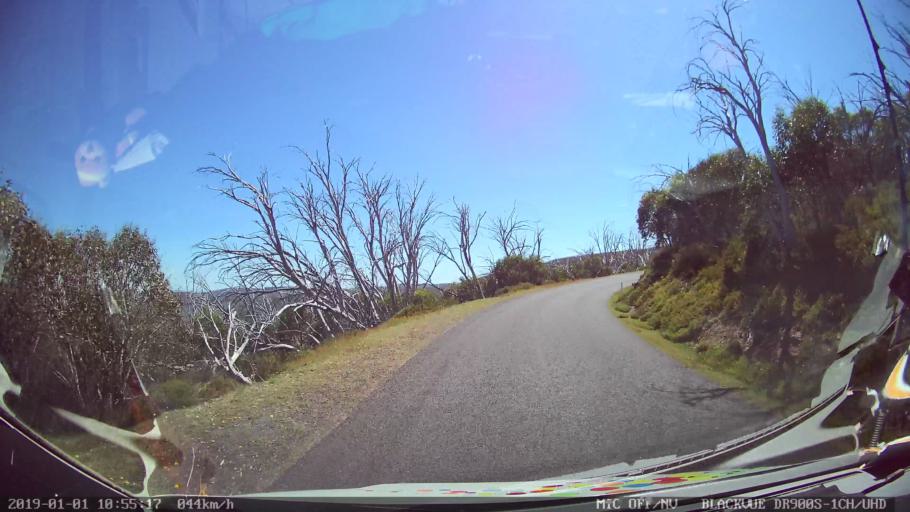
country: AU
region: New South Wales
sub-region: Snowy River
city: Jindabyne
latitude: -36.0086
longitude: 148.3876
